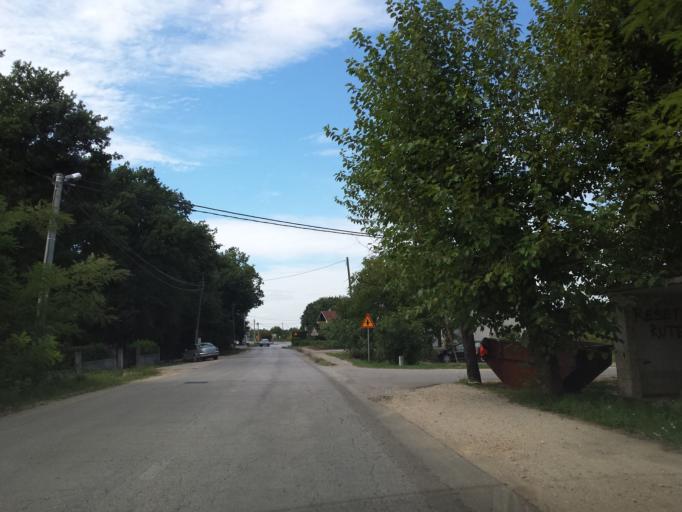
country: BA
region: Federation of Bosnia and Herzegovina
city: Citluk
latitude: 43.1909
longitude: 17.6513
